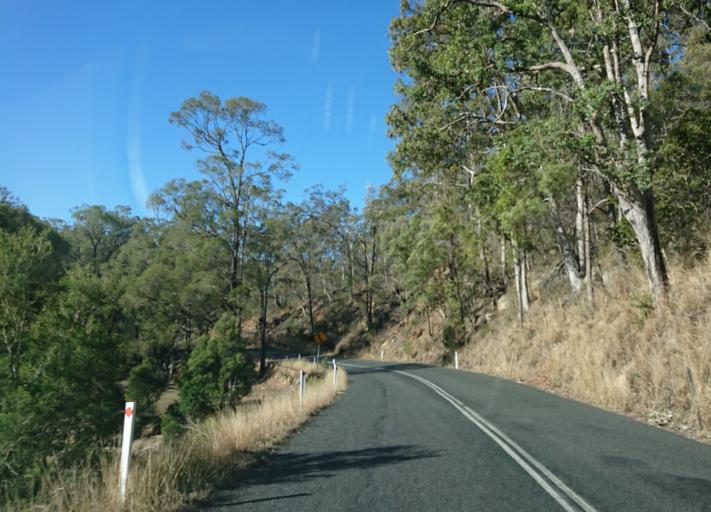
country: AU
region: Queensland
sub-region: Toowoomba
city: Top Camp
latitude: -27.7526
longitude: 152.0819
